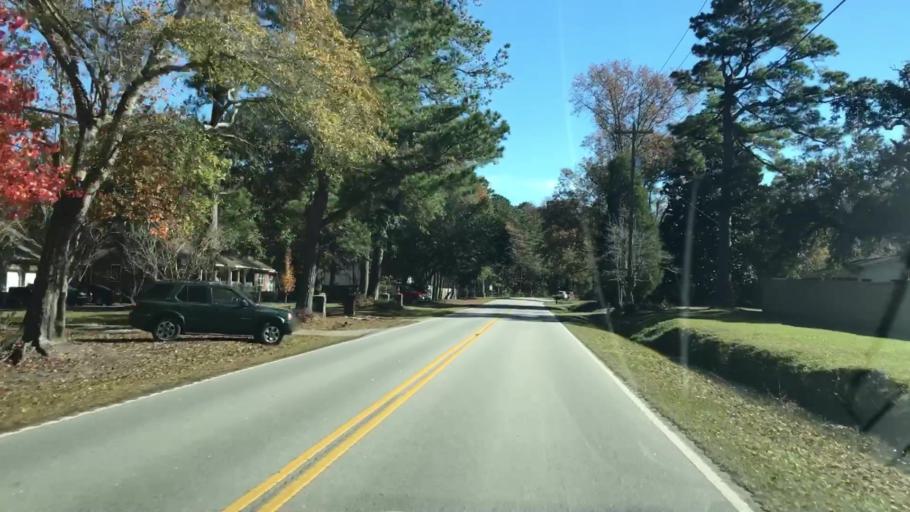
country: US
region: South Carolina
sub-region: Dorchester County
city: Summerville
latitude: 33.0207
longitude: -80.2237
